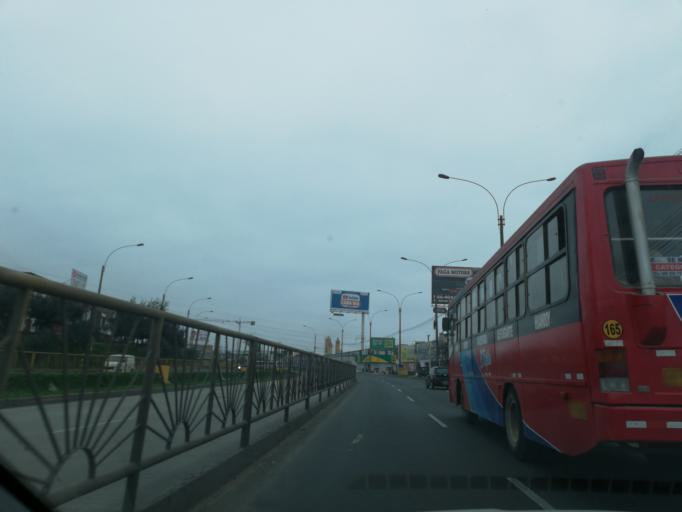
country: PE
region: Lima
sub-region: Lima
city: Independencia
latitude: -11.9915
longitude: -77.0573
